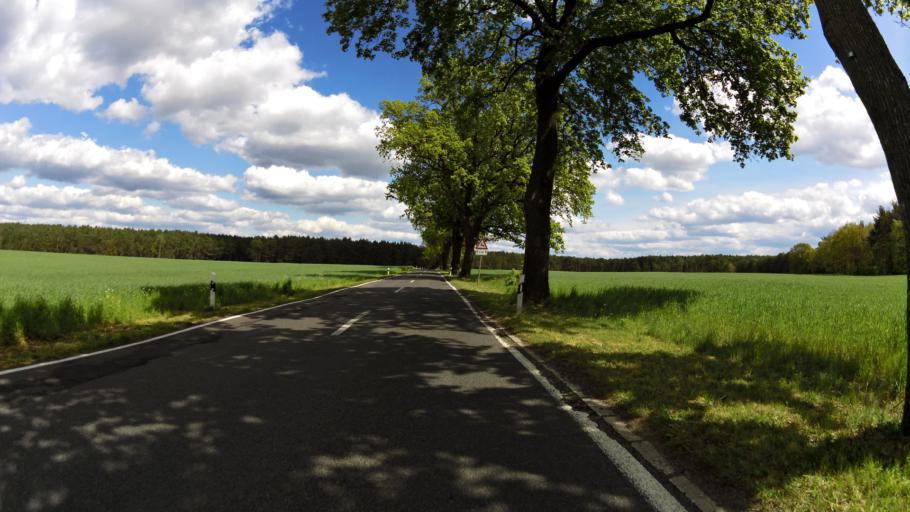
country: DE
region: Brandenburg
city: Wendisch Rietz
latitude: 52.1586
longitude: 14.0237
